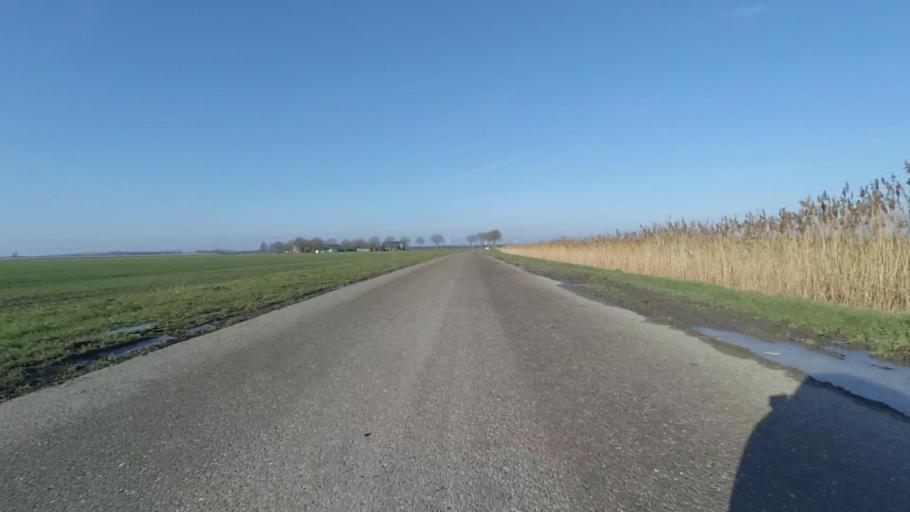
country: NL
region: Utrecht
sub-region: Gemeente Bunschoten
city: Spakenburg
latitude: 52.3051
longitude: 5.3765
